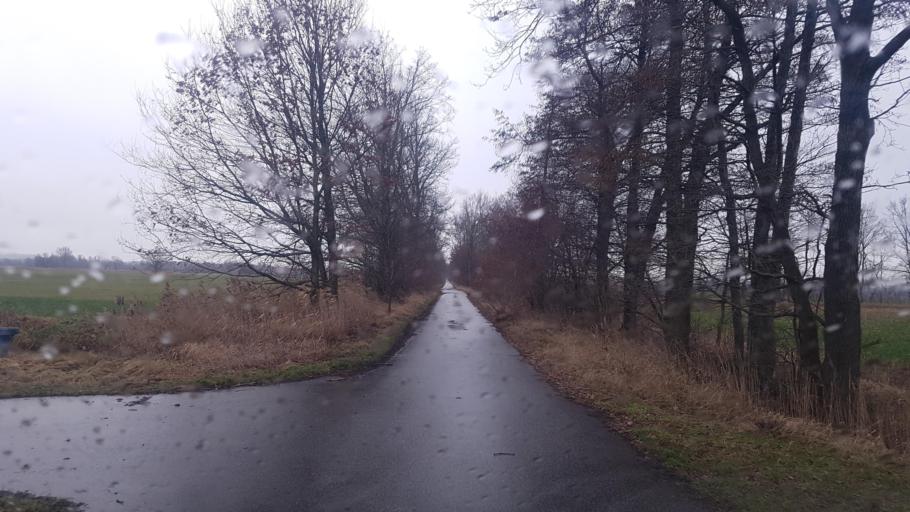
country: DE
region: Brandenburg
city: Grossthiemig
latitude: 51.4248
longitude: 13.6509
